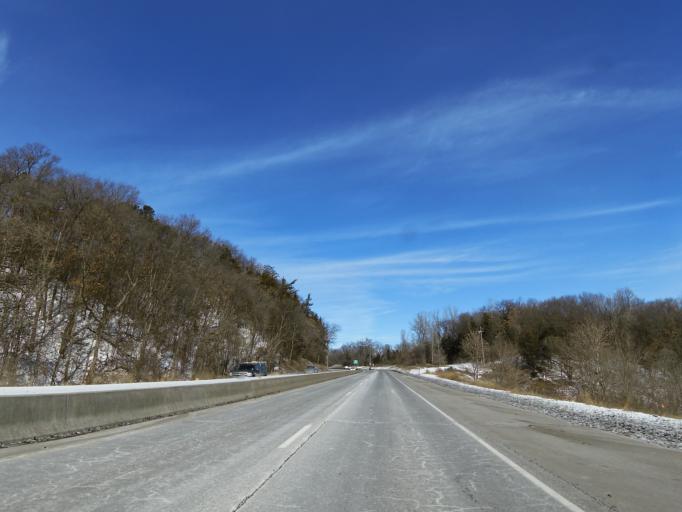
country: US
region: Minnesota
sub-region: Dakota County
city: Hastings
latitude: 44.7589
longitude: -92.8535
